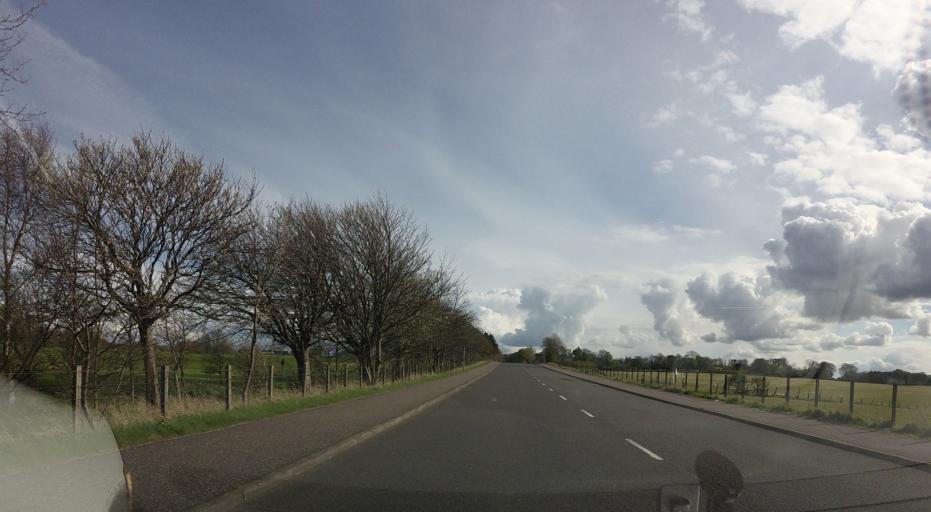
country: GB
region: Scotland
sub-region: Edinburgh
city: Colinton
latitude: 55.9773
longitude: -3.2779
